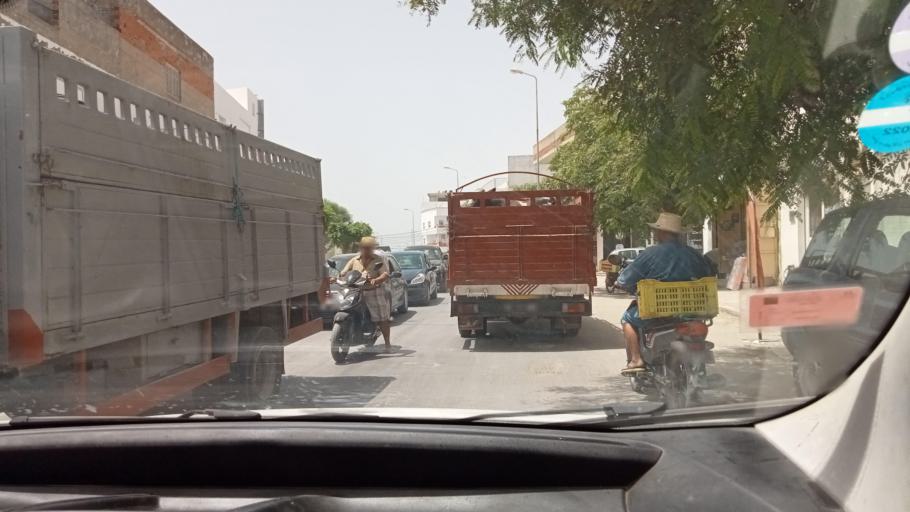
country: TN
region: Nabul
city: Qulaybiyah
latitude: 36.8476
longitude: 11.0863
